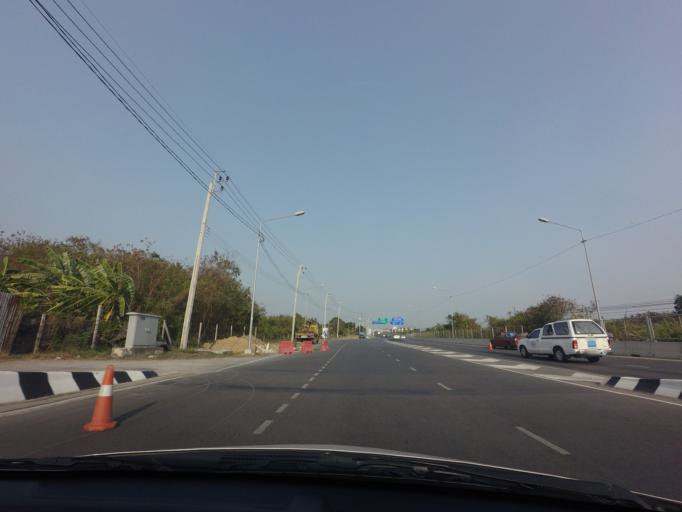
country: TH
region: Bangkok
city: Taling Chan
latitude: 13.7998
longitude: 100.4141
